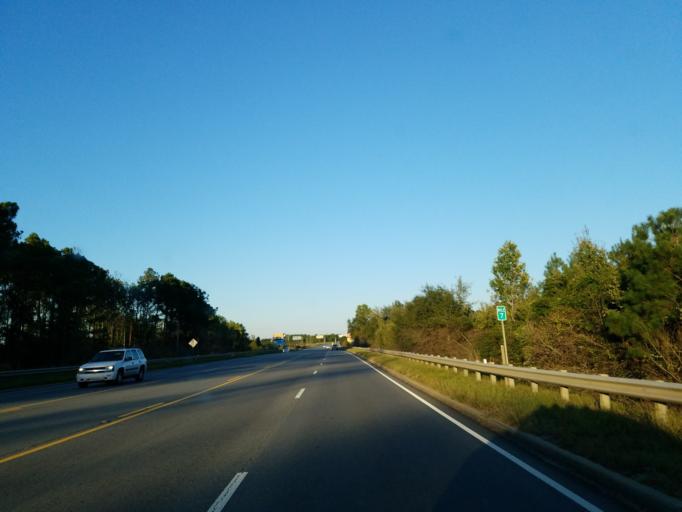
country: US
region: Georgia
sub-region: Tift County
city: Unionville
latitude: 31.4400
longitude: -83.5586
